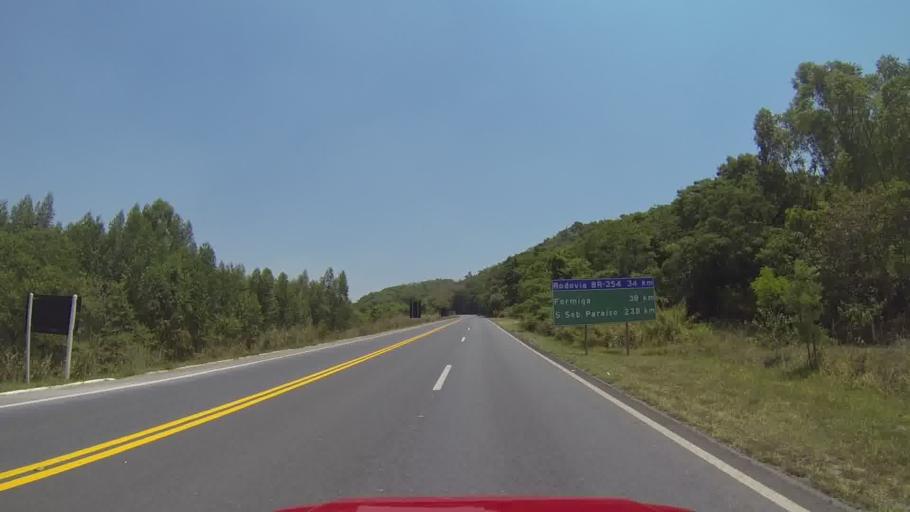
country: BR
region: Minas Gerais
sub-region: Itapecerica
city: Itapecerica
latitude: -20.2969
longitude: -45.1873
